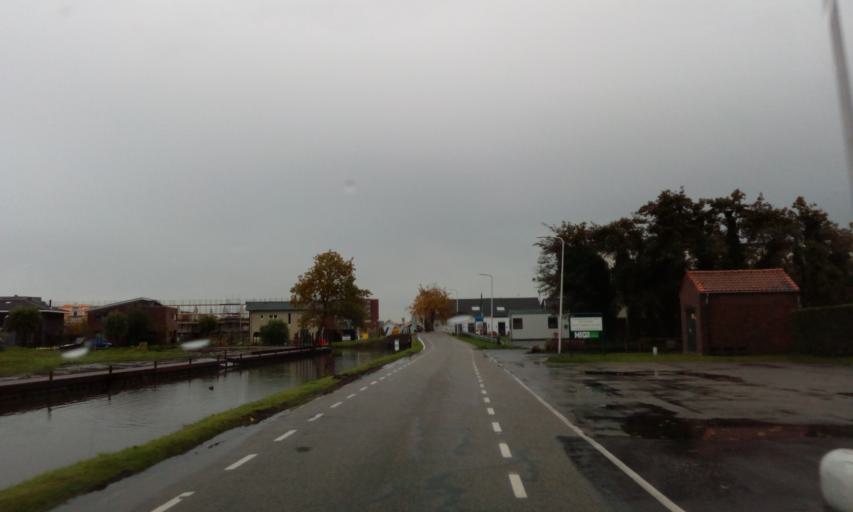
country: NL
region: South Holland
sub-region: Gemeente Rijswijk
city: Rijswijk
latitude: 52.0135
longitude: 4.3249
